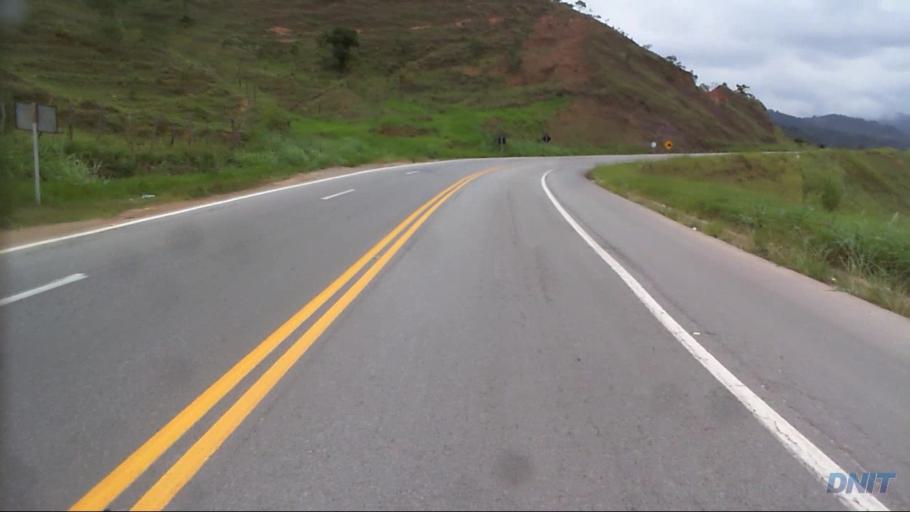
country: BR
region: Minas Gerais
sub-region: Nova Era
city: Nova Era
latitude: -19.6407
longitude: -42.9003
